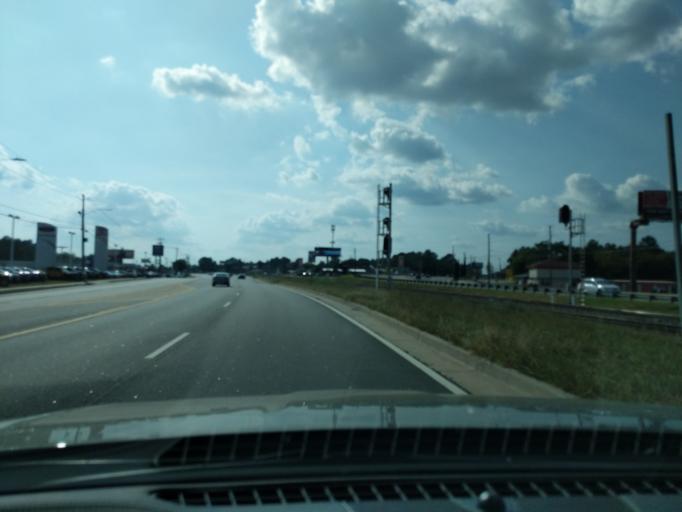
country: US
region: Georgia
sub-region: Columbia County
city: Martinez
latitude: 33.5165
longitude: -82.0728
